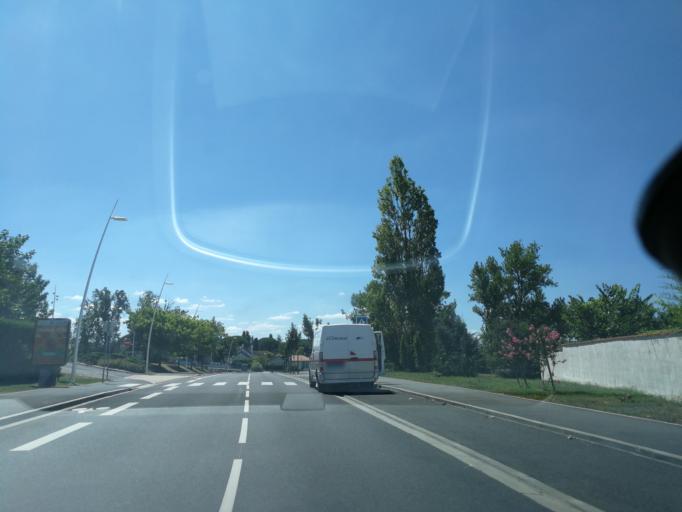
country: FR
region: Midi-Pyrenees
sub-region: Departement de la Haute-Garonne
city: Balma
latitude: 43.6071
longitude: 1.5020
